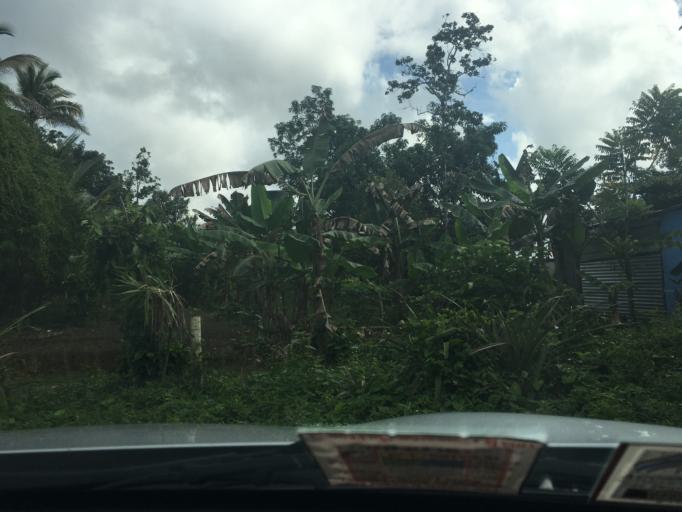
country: BZ
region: Cayo
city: Belmopan
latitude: 17.2470
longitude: -88.7923
